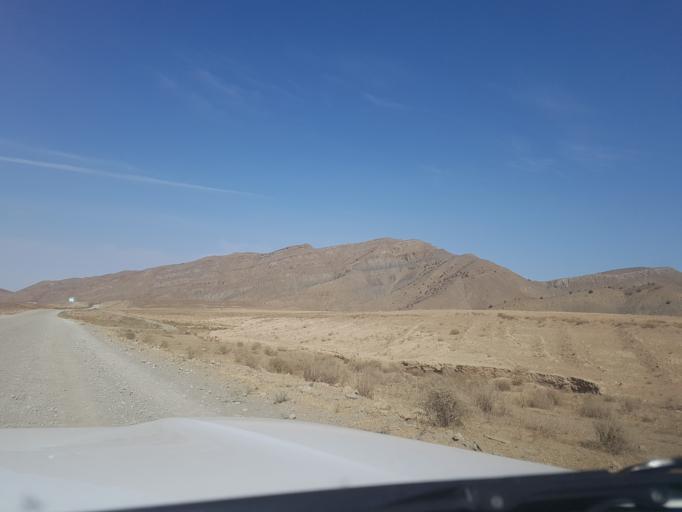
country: TM
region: Ahal
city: Baharly
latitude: 38.4380
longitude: 57.0408
